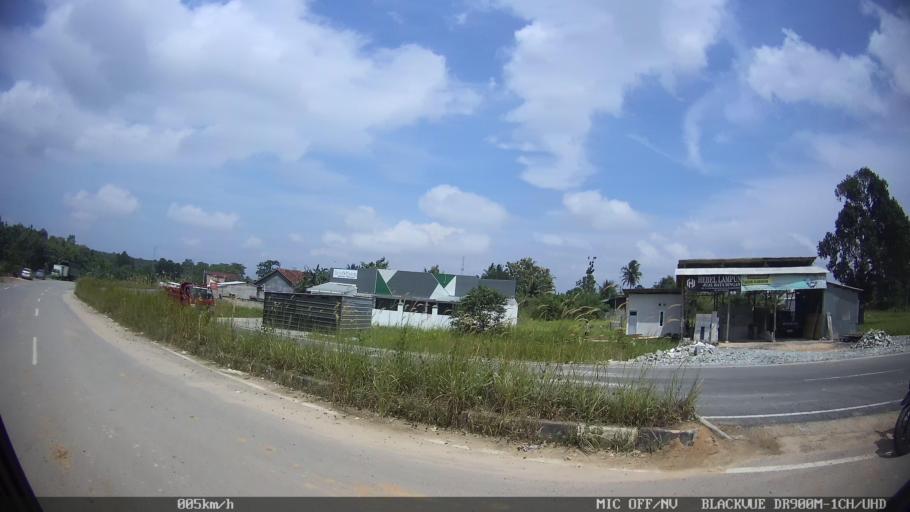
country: ID
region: Lampung
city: Kedaton
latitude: -5.3503
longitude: 105.3257
